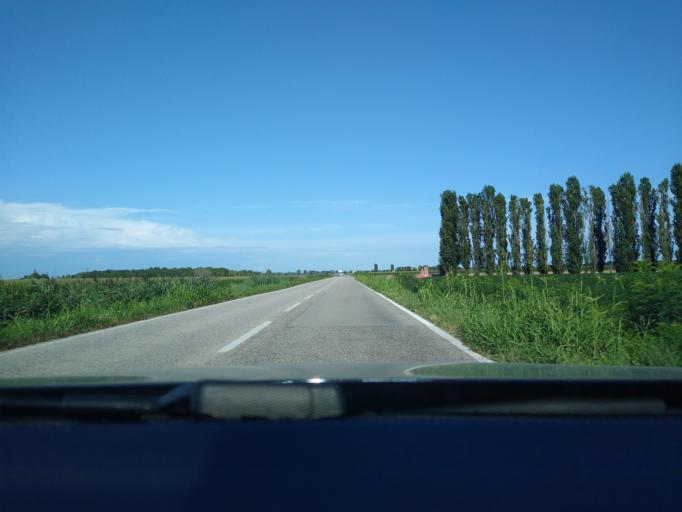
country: IT
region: Veneto
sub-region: Provincia di Venezia
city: La Salute di Livenza
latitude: 45.6849
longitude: 12.8383
